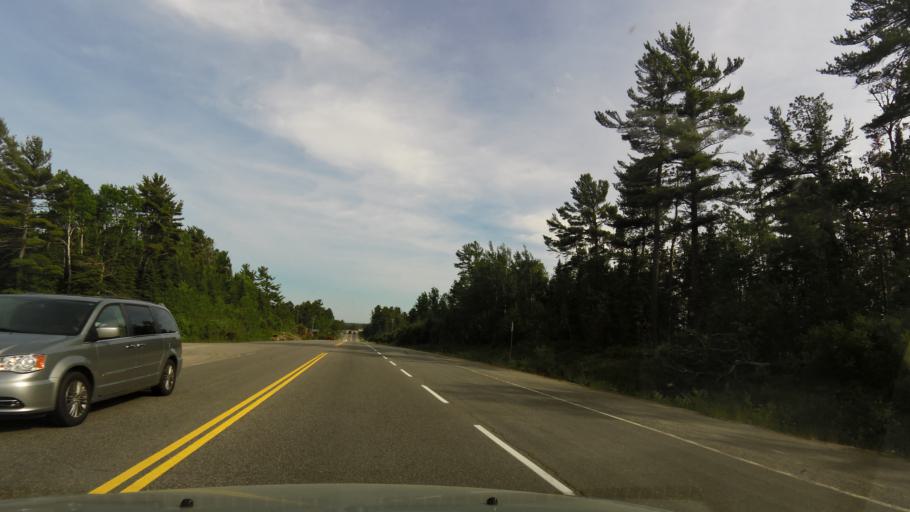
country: CA
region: Ontario
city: Greater Sudbury
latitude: 46.0080
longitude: -80.5741
